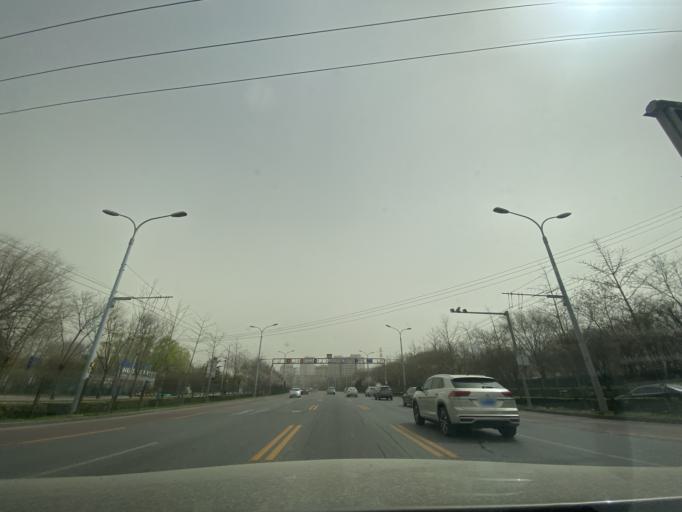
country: CN
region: Beijing
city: Sijiqing
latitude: 39.9453
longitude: 116.2769
